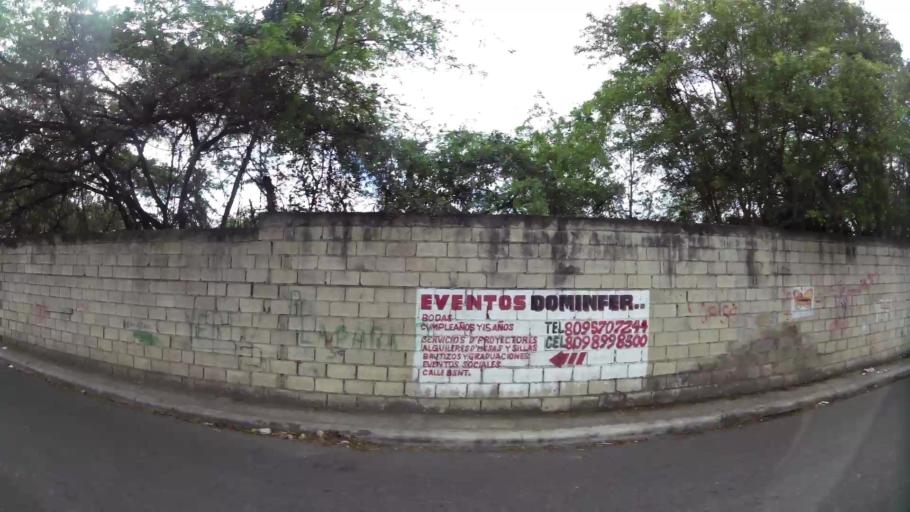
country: DO
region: Santiago
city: Santiago de los Caballeros
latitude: 19.4263
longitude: -70.6632
